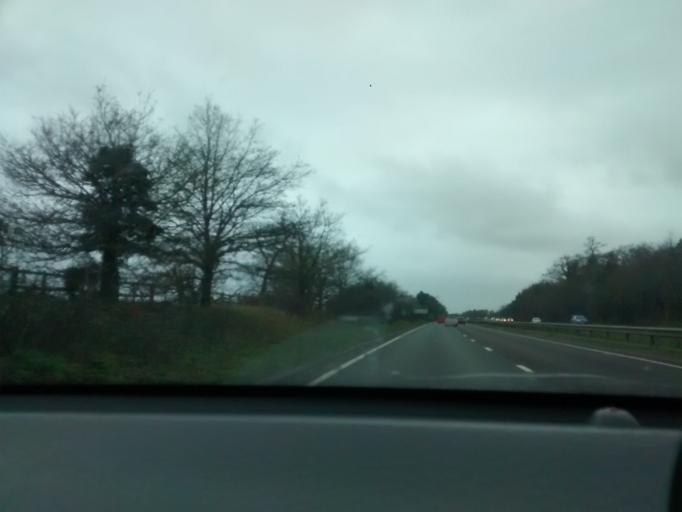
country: GB
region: England
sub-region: Suffolk
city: Needham Market
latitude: 52.1387
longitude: 1.0857
